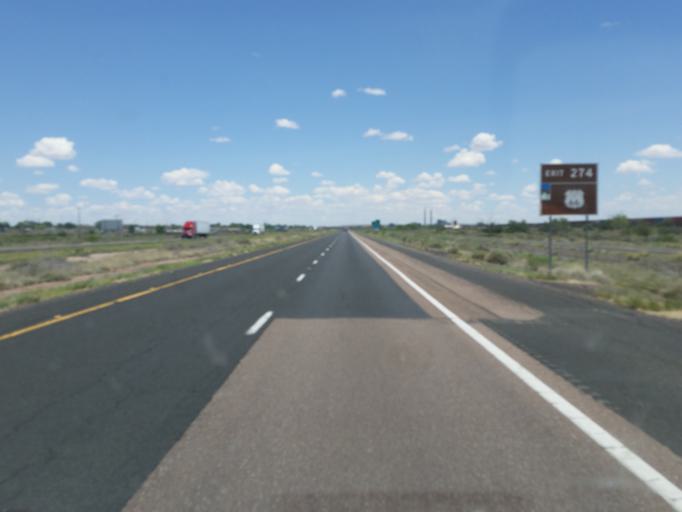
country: US
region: Arizona
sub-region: Navajo County
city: Joseph City
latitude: 34.9590
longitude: -110.3701
